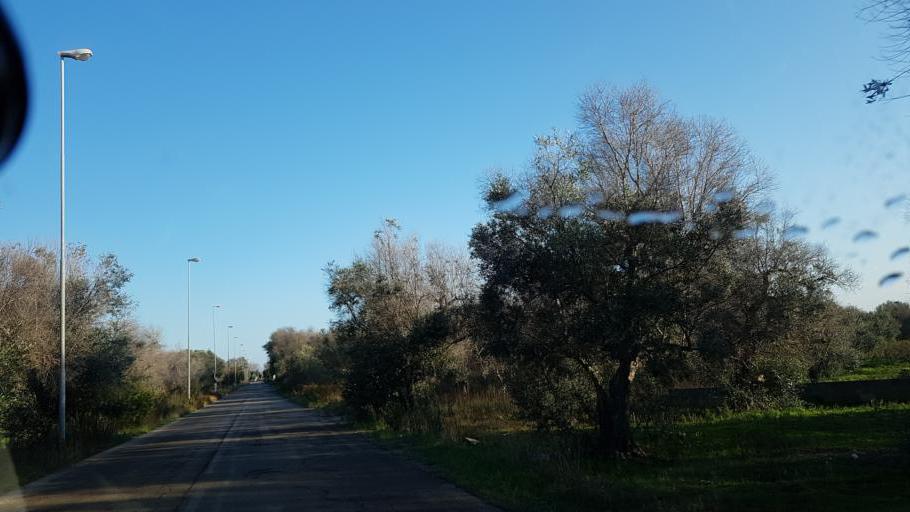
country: IT
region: Apulia
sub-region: Provincia di Brindisi
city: Torchiarolo
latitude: 40.5050
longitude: 18.1025
